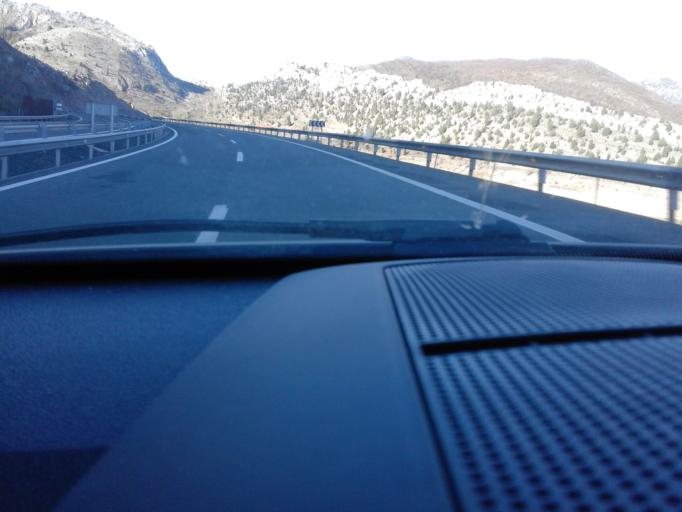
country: ES
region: Castille and Leon
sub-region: Provincia de Leon
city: Sena de Luna
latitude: 42.8795
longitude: -5.8822
